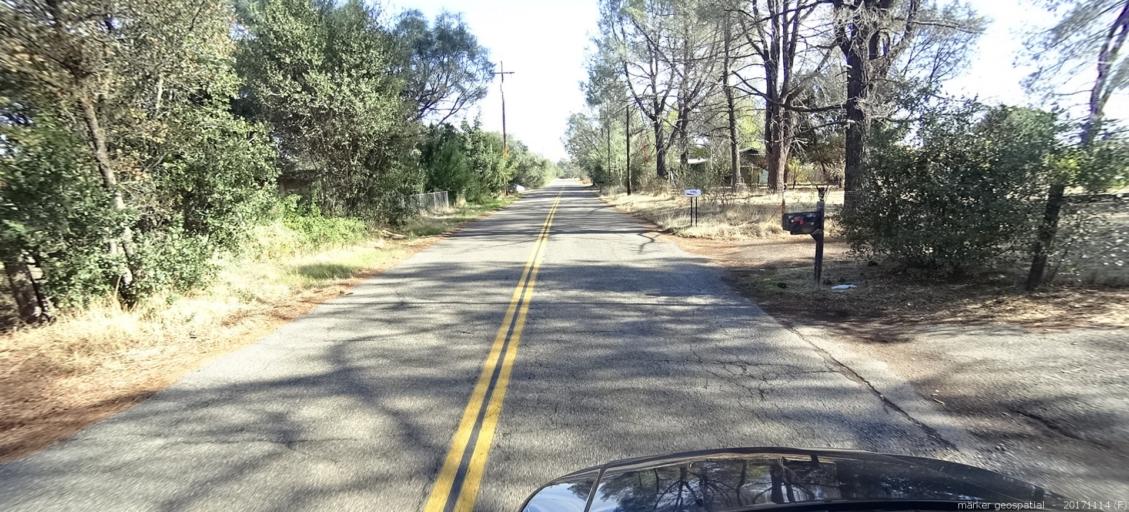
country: US
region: California
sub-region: Shasta County
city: Anderson
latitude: 40.4321
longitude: -122.4124
